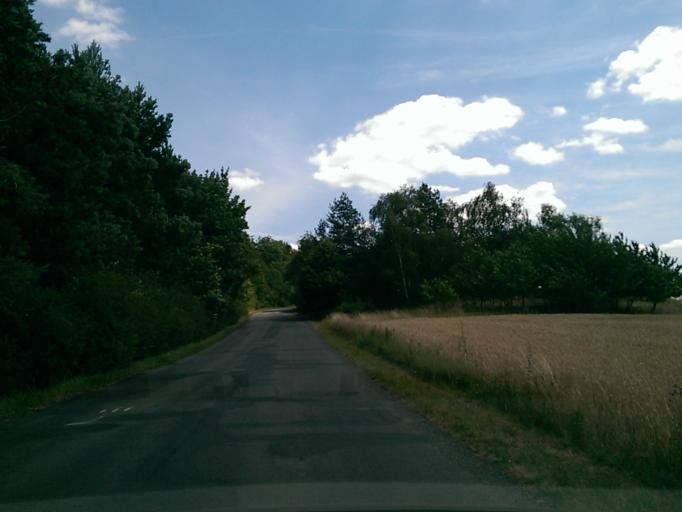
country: CZ
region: Central Bohemia
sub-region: Okres Melnik
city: Melnik
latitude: 50.3793
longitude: 14.4915
